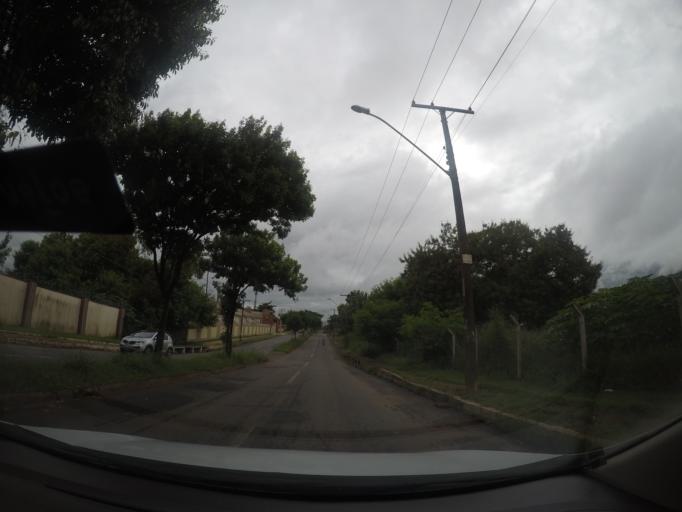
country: BR
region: Goias
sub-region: Goiania
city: Goiania
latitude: -16.7311
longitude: -49.2830
